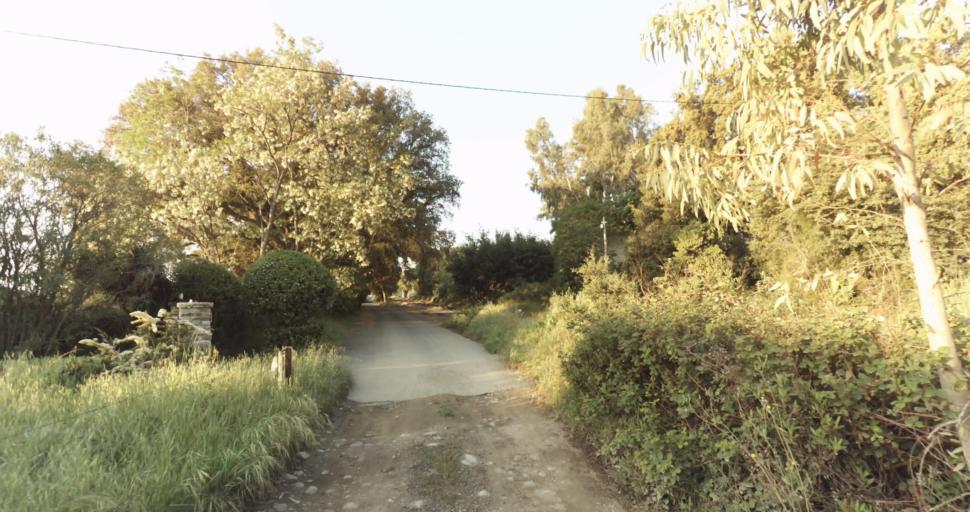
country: FR
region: Corsica
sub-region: Departement de la Haute-Corse
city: Biguglia
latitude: 42.6315
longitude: 9.4406
